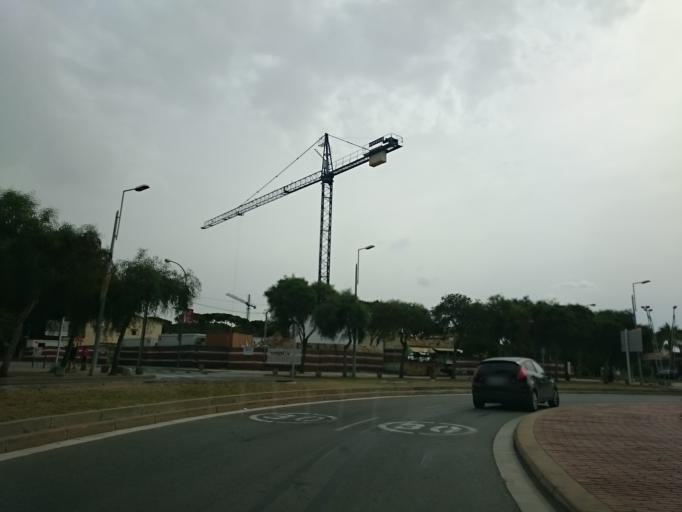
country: ES
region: Catalonia
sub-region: Provincia de Barcelona
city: Castelldefels
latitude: 41.2656
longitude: 1.9916
